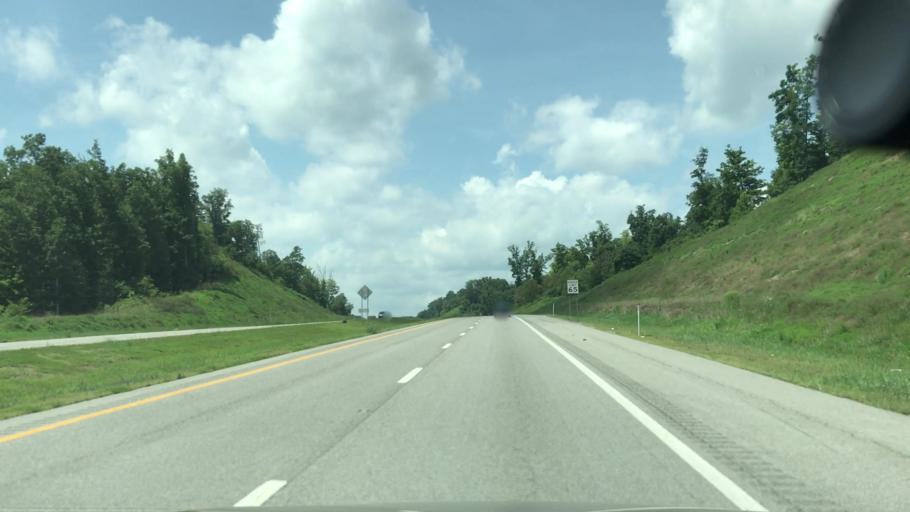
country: US
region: West Virginia
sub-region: Mason County
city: Point Pleasant
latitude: 38.7829
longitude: -82.0735
